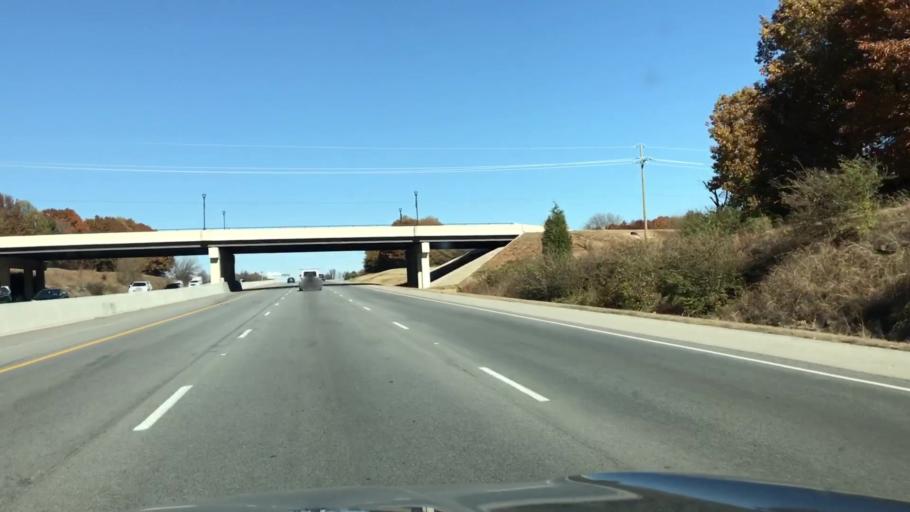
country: US
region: Arkansas
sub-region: Benton County
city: Lowell
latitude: 36.2529
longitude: -94.1503
